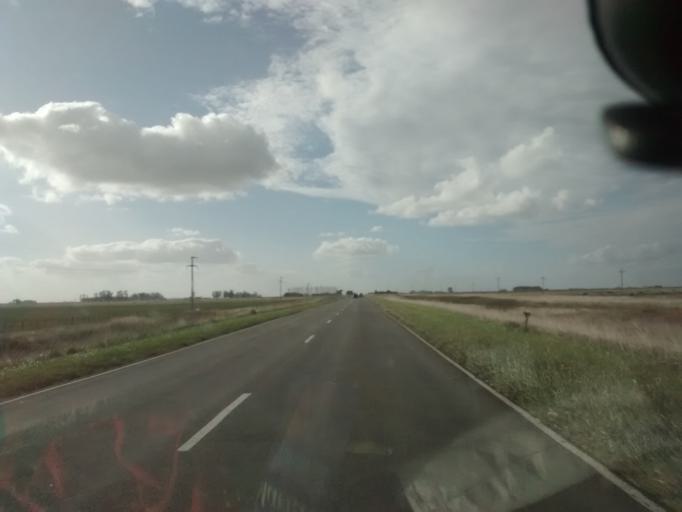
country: AR
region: Buenos Aires
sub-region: Partido de Ayacucho
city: Ayacucho
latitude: -36.9089
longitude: -58.5266
